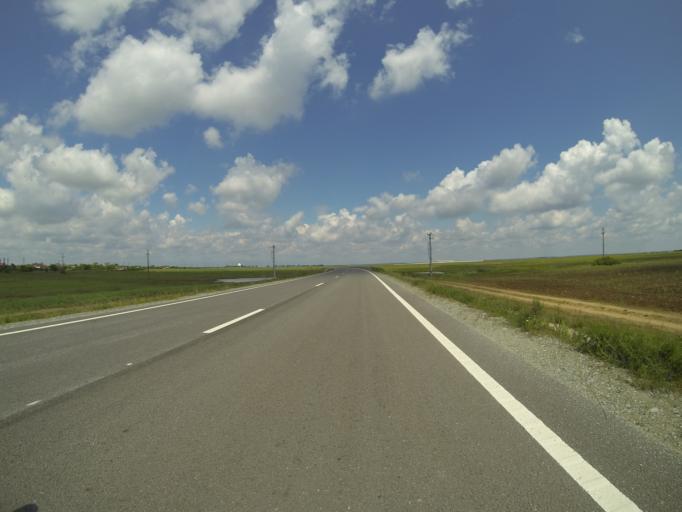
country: RO
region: Dolj
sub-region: Comuna Carcea
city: Carcea
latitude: 44.2636
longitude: 23.9090
